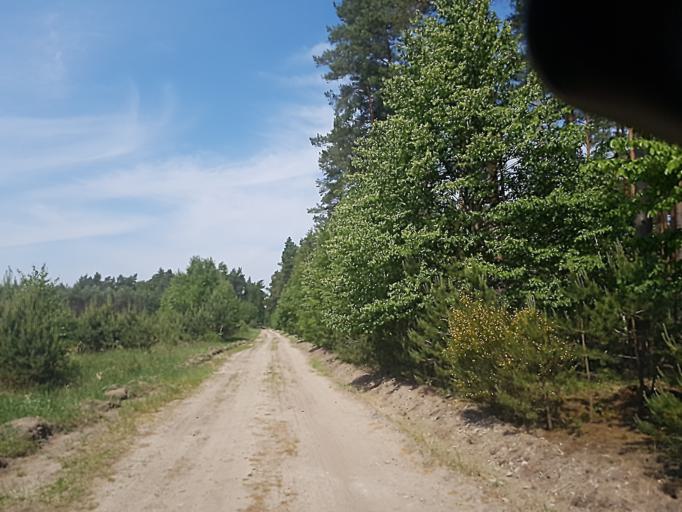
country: DE
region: Brandenburg
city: Gorzke
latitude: 52.0963
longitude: 12.3251
